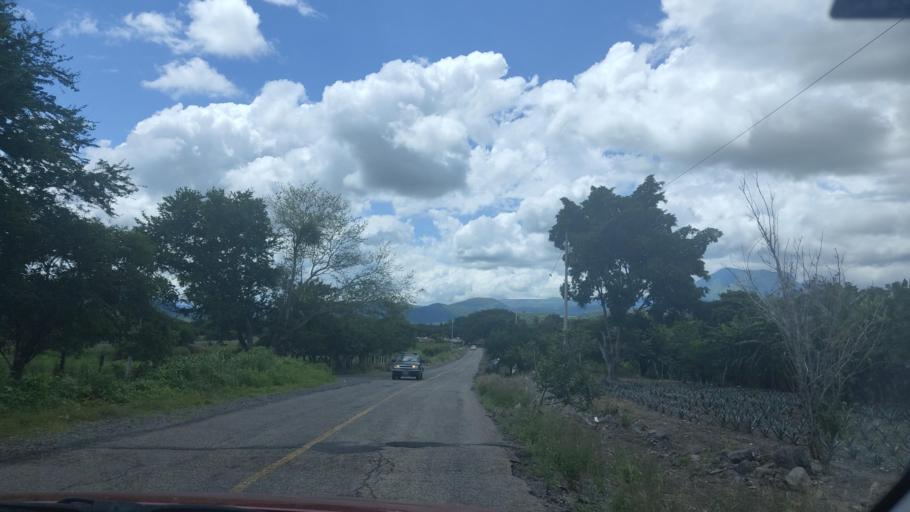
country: MX
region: Nayarit
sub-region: Ahuacatlan
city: Ahuacatlan
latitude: 21.1281
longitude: -104.6069
